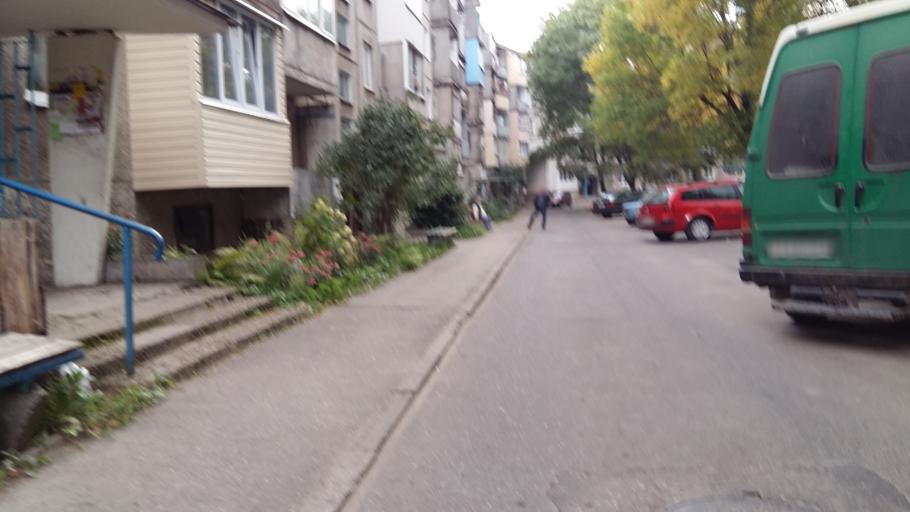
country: BY
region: Grodnenskaya
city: Hrodna
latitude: 53.7037
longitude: 23.7973
